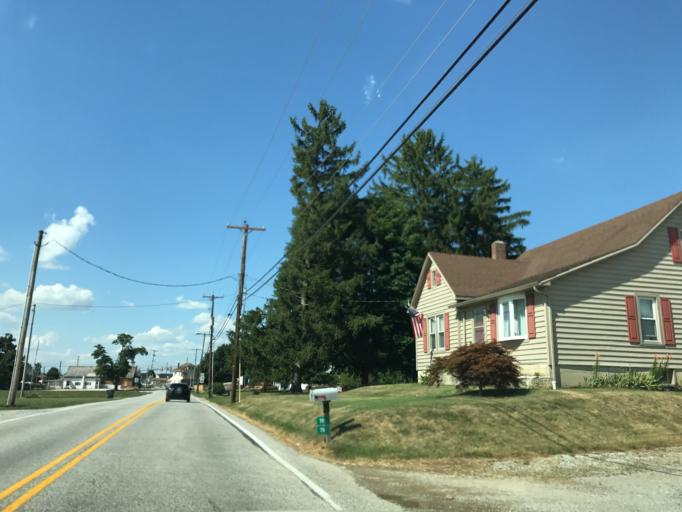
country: US
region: Pennsylvania
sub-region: Adams County
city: McSherrystown
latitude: 39.7946
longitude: -77.0405
